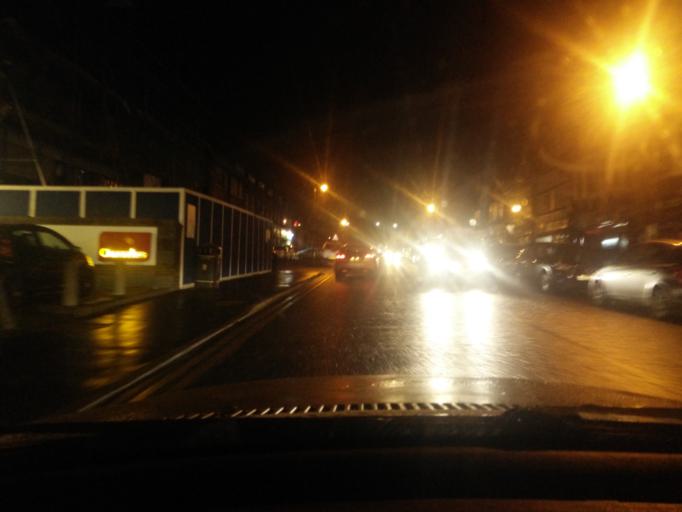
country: GB
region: England
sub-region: Buckinghamshire
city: Amersham on the Hill
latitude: 51.6756
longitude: -0.6076
